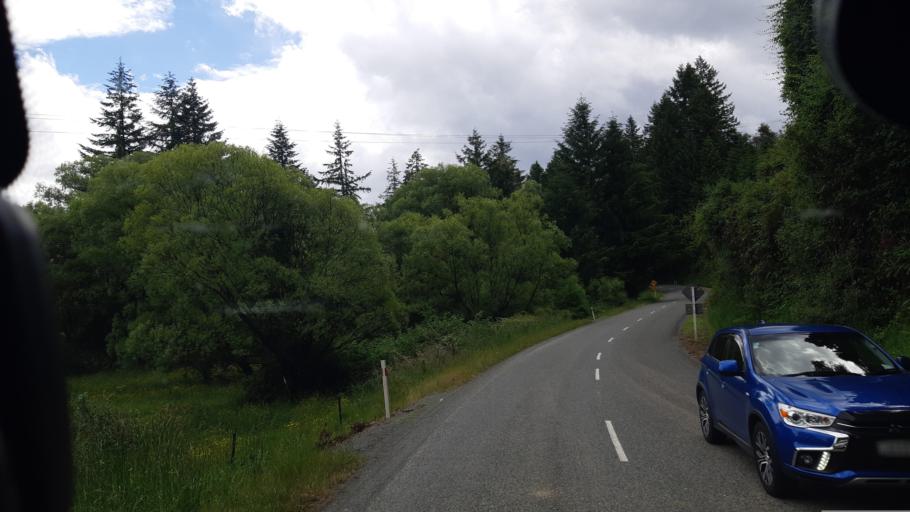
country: NZ
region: Tasman
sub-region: Tasman District
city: Wakefield
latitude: -41.6124
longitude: 172.8005
